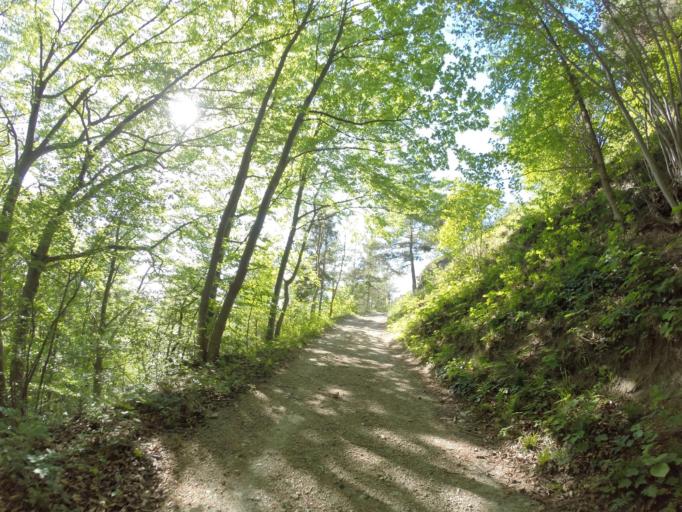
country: DE
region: Thuringia
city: Golmsdorf
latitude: 50.9566
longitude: 11.6517
